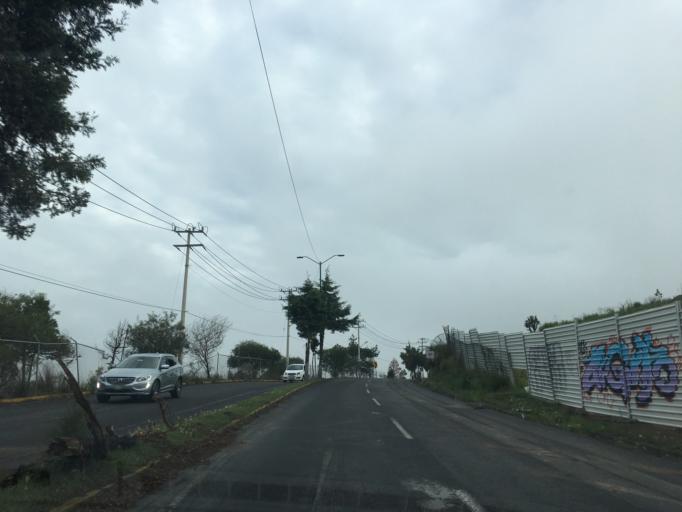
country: MX
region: Mexico
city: Ciudad Lopez Mateos
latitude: 19.5398
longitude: -99.2650
